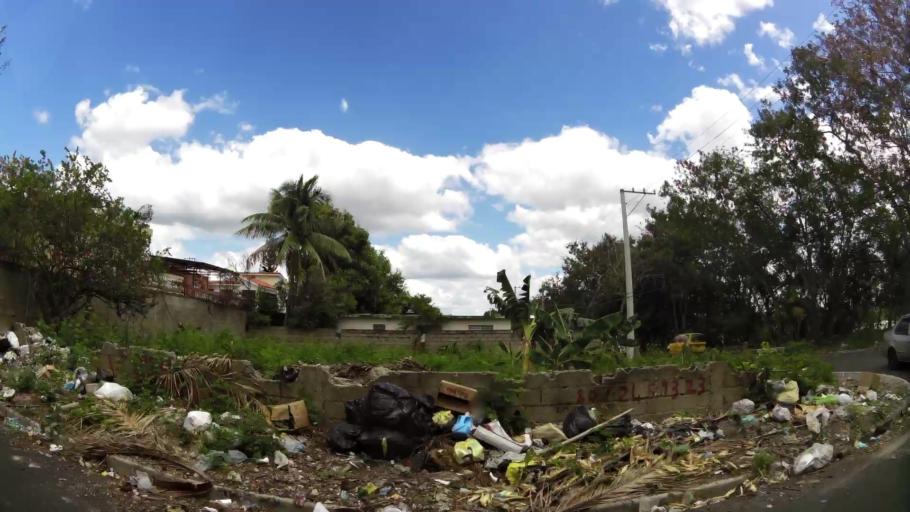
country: DO
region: Nacional
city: Ensanche Luperon
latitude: 18.5163
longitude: -69.9067
